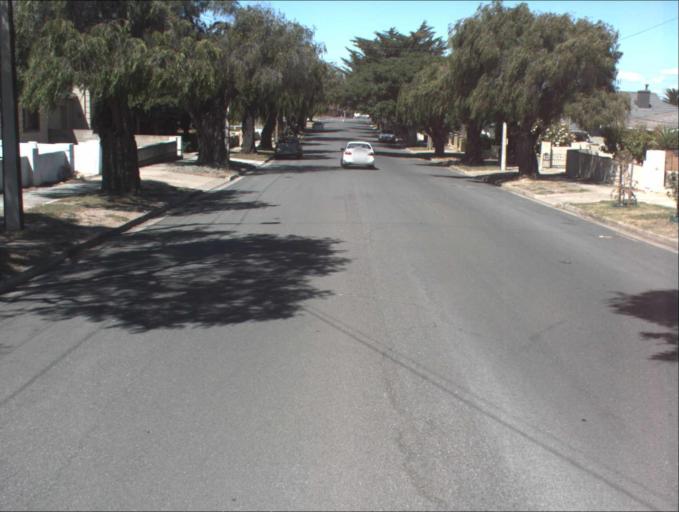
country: AU
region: South Australia
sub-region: Port Adelaide Enfield
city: Birkenhead
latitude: -34.8152
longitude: 138.4918
